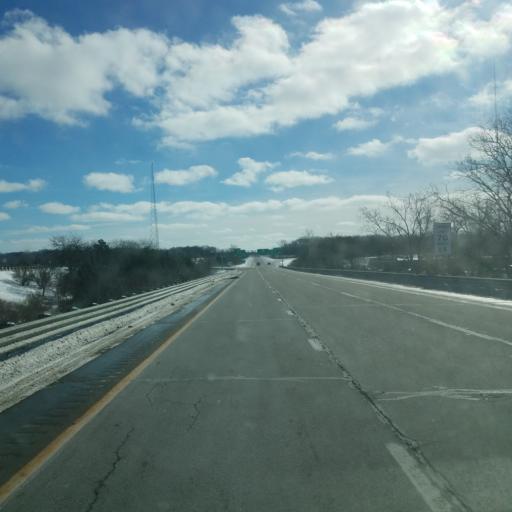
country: US
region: Michigan
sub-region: Ingham County
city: Holt
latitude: 42.6819
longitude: -84.5005
